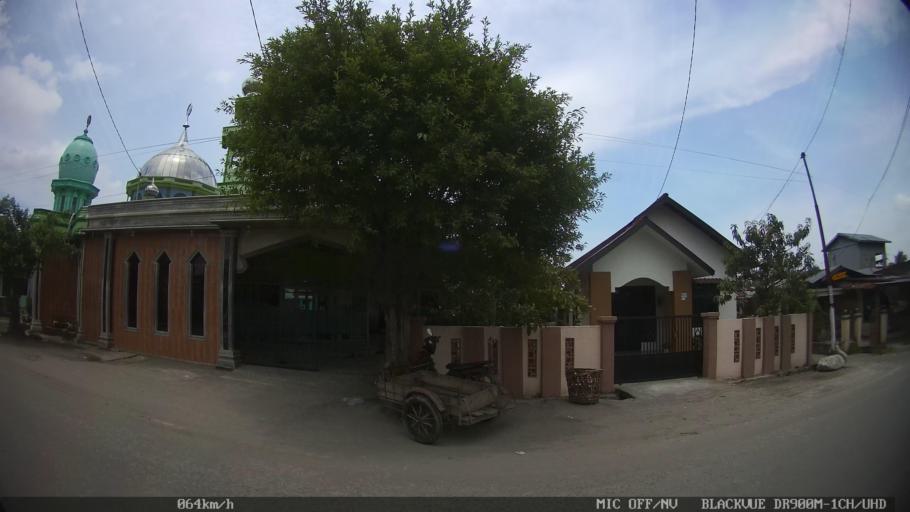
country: ID
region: North Sumatra
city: Labuhan Deli
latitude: 3.6773
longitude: 98.6725
